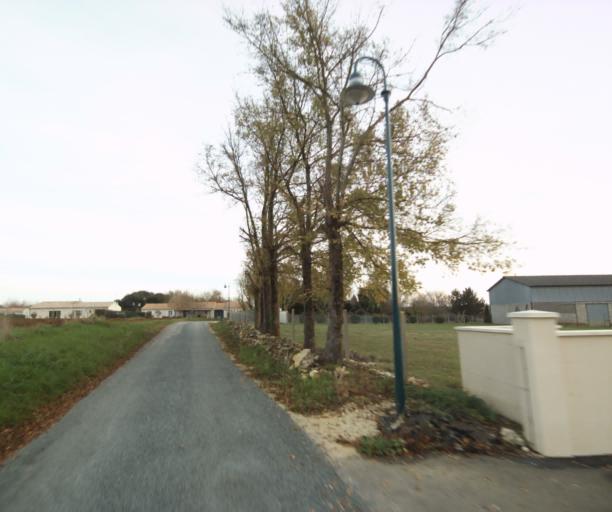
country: FR
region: Poitou-Charentes
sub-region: Departement de la Charente-Maritime
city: Bussac-sur-Charente
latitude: 45.8126
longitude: -0.6102
